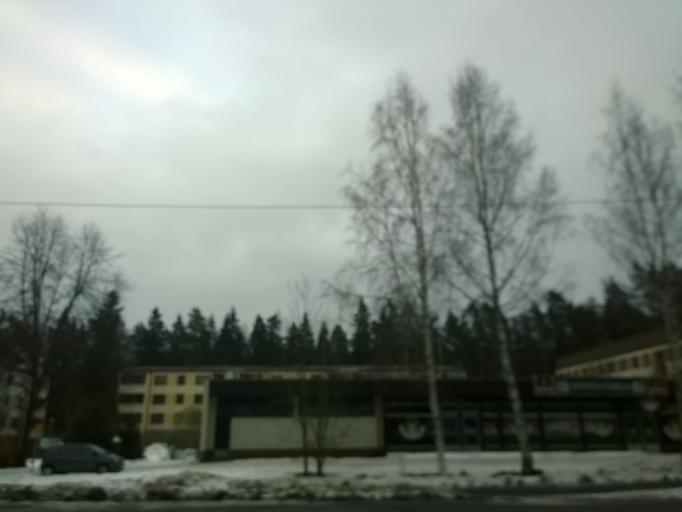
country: FI
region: Pirkanmaa
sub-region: Tampere
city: Tampere
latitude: 61.4102
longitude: 23.7616
